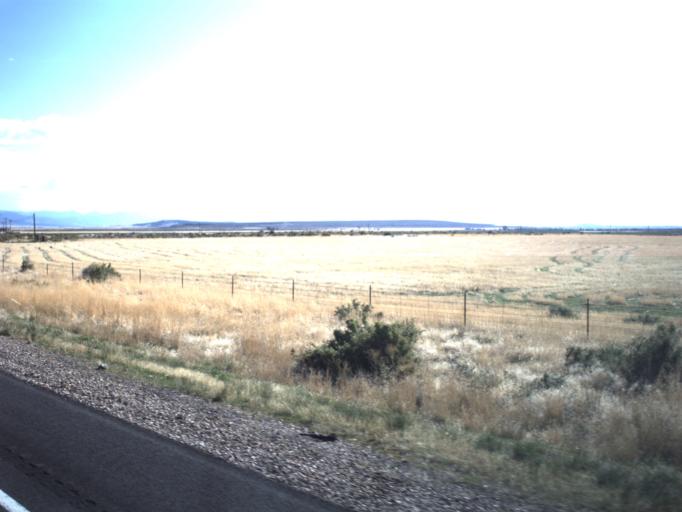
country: US
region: Utah
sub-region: Millard County
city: Fillmore
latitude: 39.1240
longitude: -112.3580
